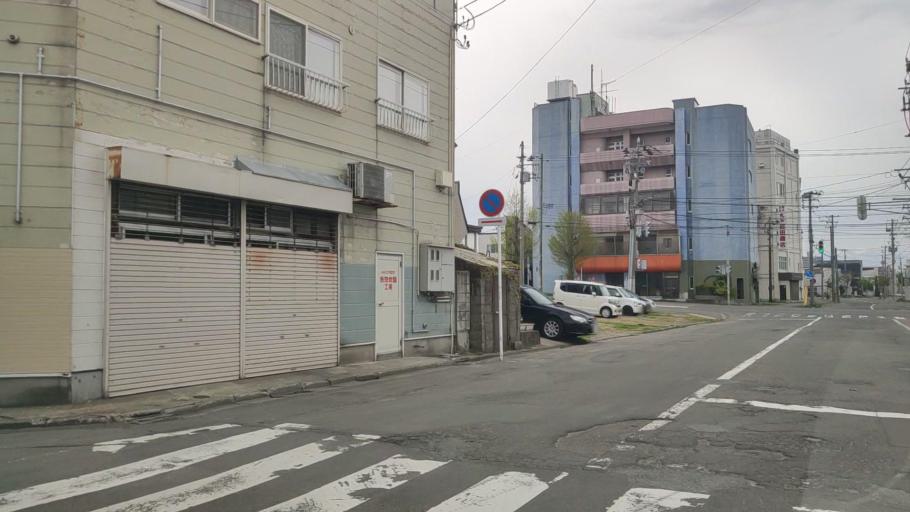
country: JP
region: Aomori
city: Aomori Shi
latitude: 40.8294
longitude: 140.7590
